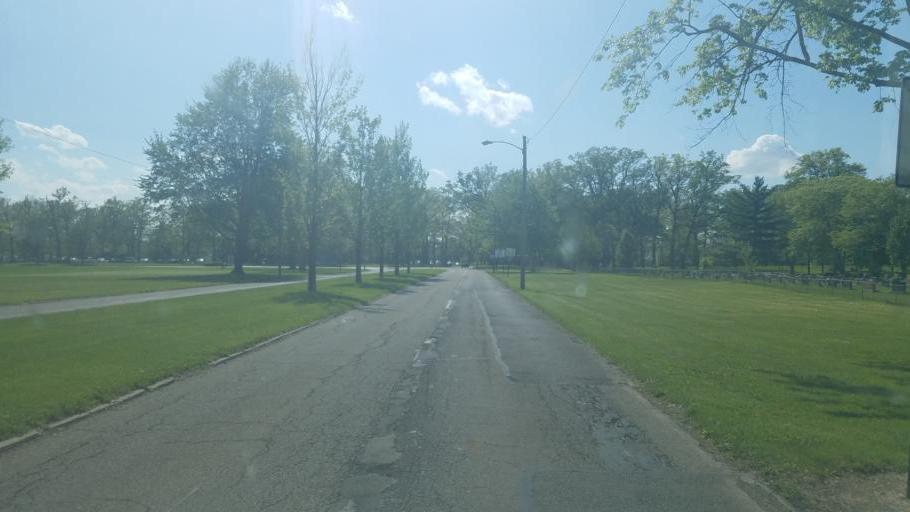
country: US
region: Ohio
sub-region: Marion County
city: Marion
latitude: 40.5744
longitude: -83.1268
